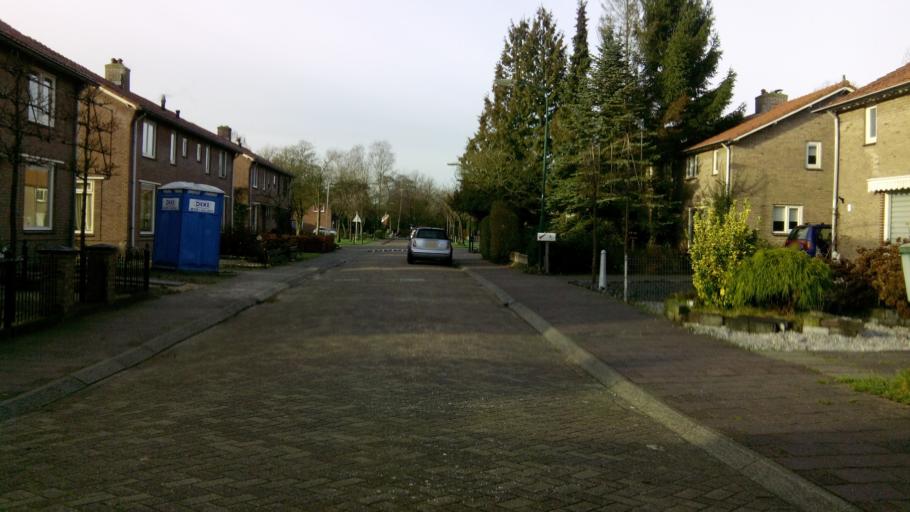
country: NL
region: Utrecht
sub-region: Gemeente Leusden
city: Leusden
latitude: 52.1148
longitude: 5.4068
